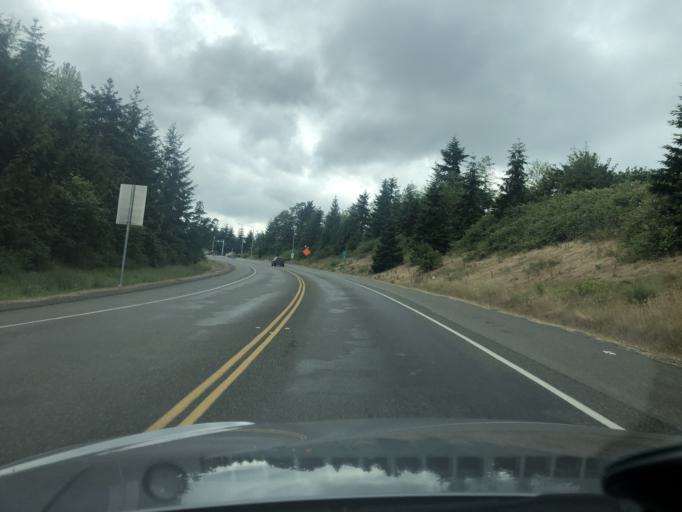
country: US
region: Washington
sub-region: King County
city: Lea Hill
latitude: 47.3308
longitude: -122.1611
